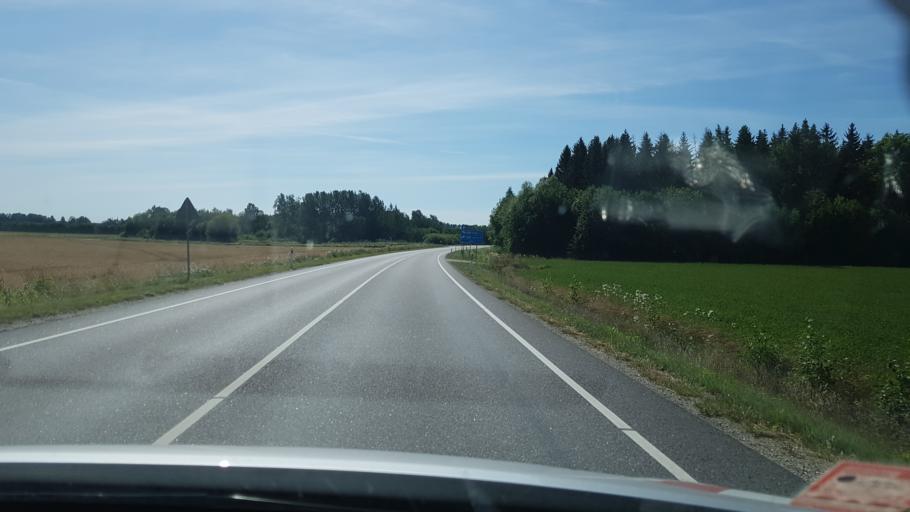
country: EE
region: Tartu
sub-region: Tartu linn
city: Tartu
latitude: 58.4076
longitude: 26.8953
